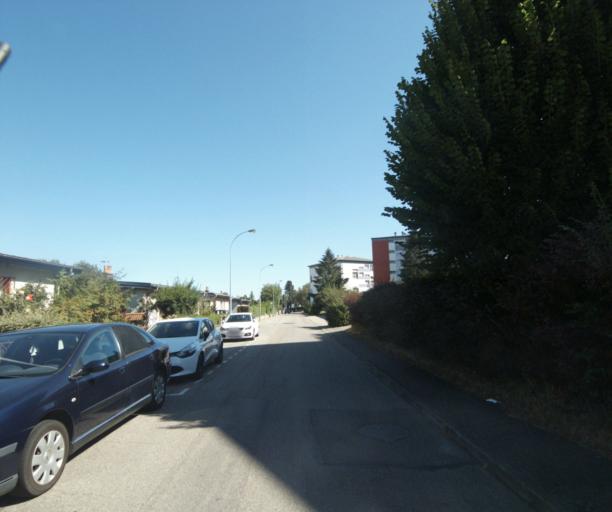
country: FR
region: Lorraine
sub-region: Departement des Vosges
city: Epinal
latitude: 48.1841
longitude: 6.4527
